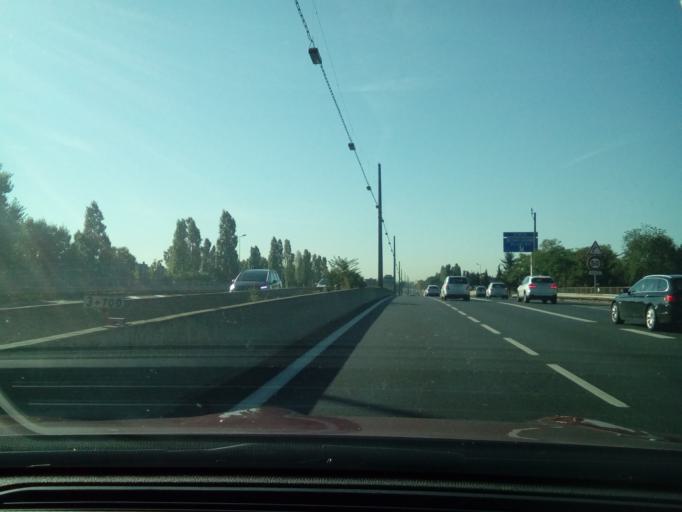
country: FR
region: Rhone-Alpes
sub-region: Departement du Rhone
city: Villeurbanne
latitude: 45.7838
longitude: 4.8914
